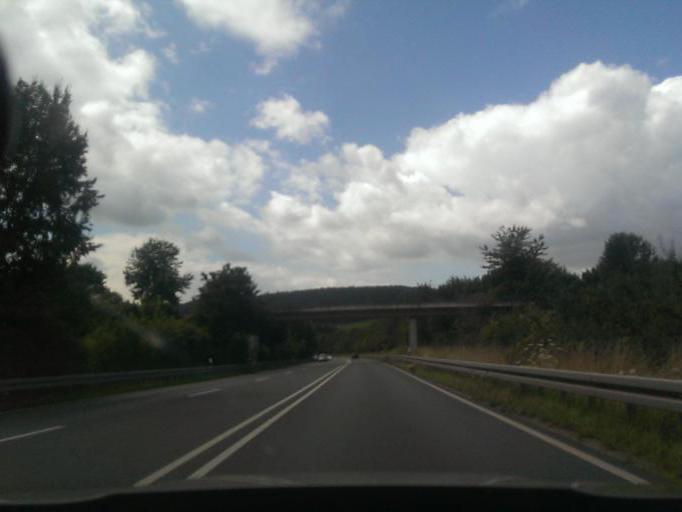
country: DE
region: Lower Saxony
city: Holzminden
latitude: 51.8191
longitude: 9.4108
